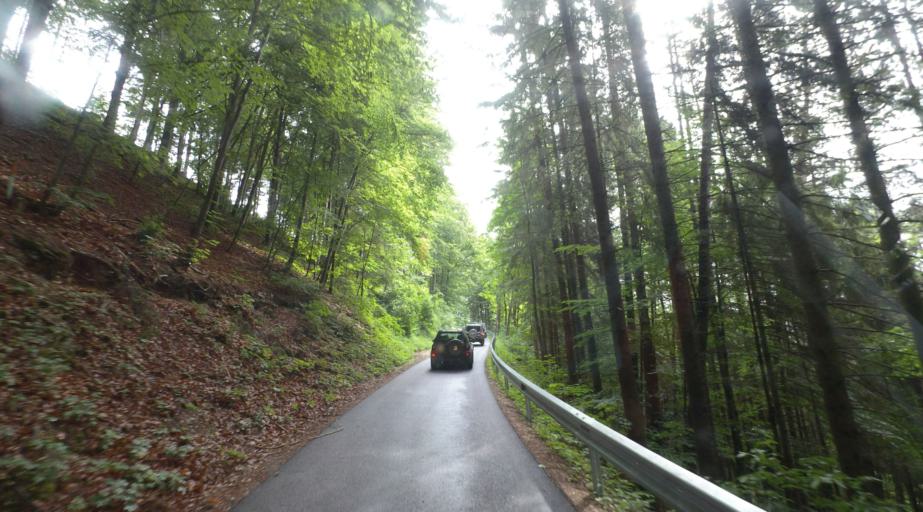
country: AT
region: Upper Austria
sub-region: Politischer Bezirk Kirchdorf an der Krems
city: Micheldorf in Oberoesterreich
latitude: 47.8941
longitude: 14.2150
